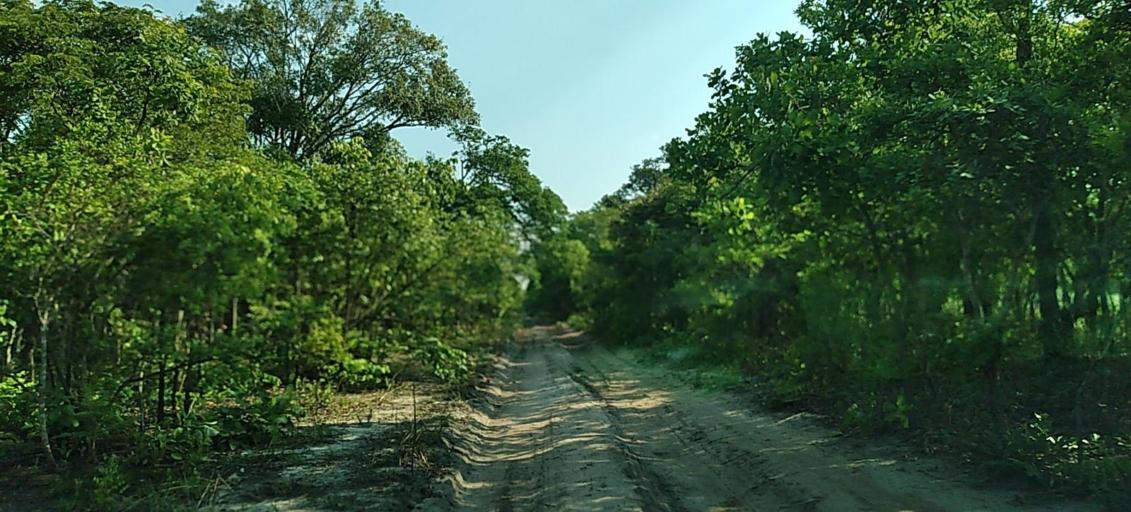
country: ZM
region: North-Western
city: Mwinilunga
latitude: -11.3189
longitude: 24.7396
